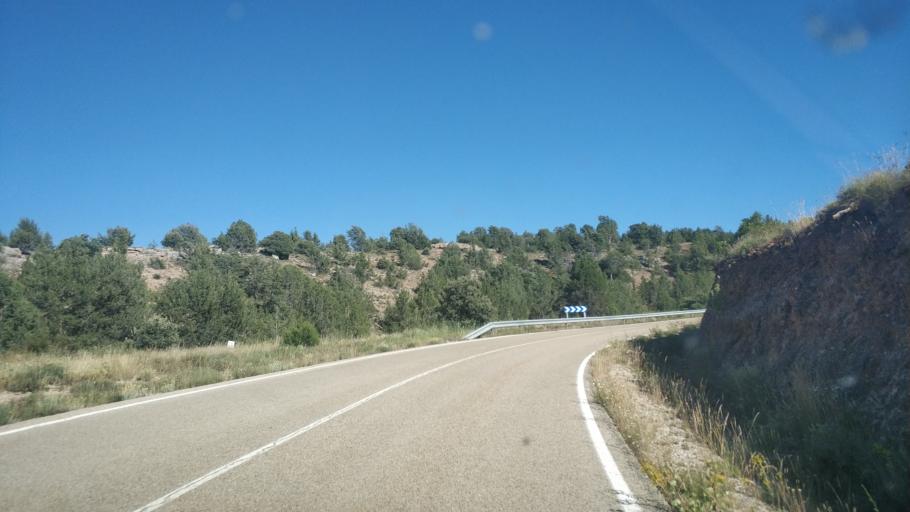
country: ES
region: Castille and Leon
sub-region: Provincia de Soria
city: Montejo de Tiermes
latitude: 41.4296
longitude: -3.2033
